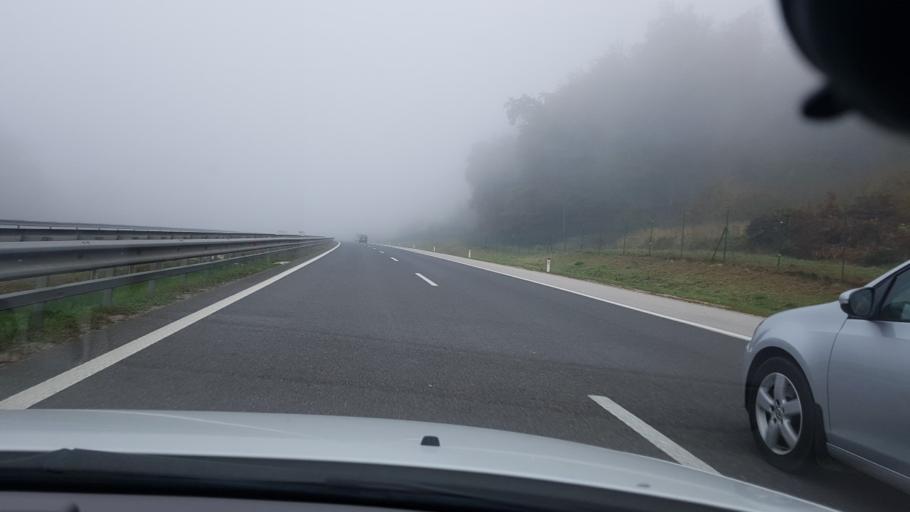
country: SI
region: Mirna Pec
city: Mirna Pec
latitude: 45.8823
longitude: 15.0768
